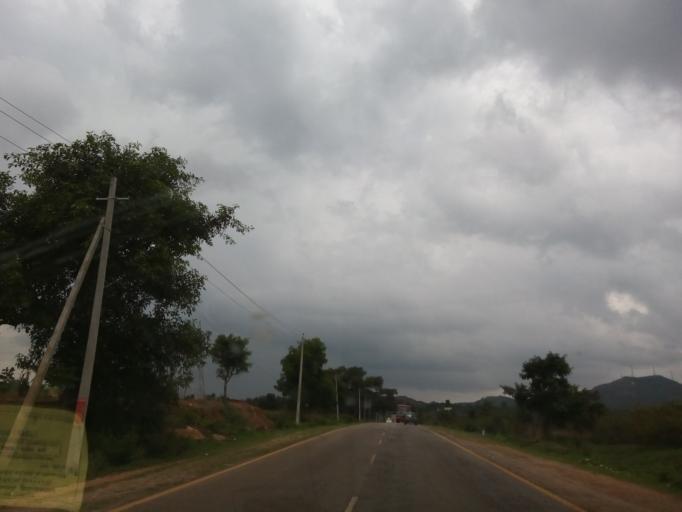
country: IN
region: Karnataka
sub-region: Hassan
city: Hassan
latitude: 13.0723
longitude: 76.0483
